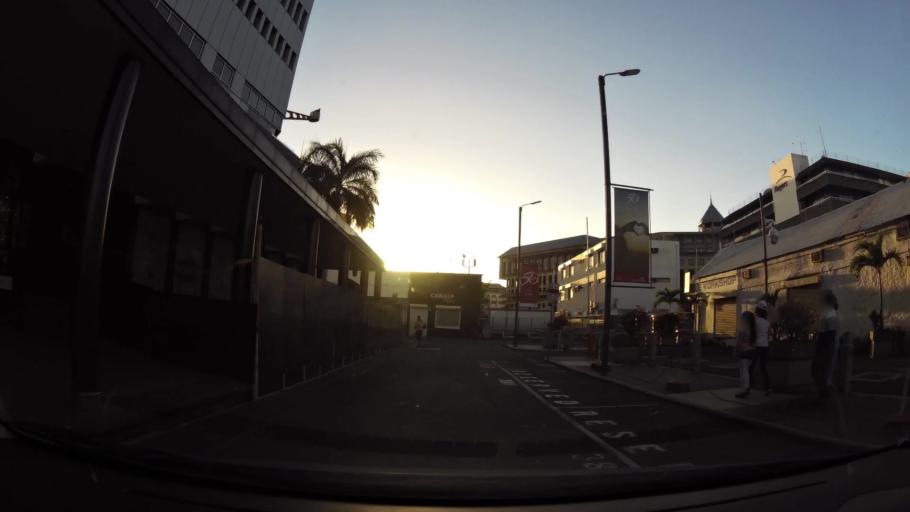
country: MU
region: Port Louis
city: Port Louis
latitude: -20.1629
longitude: 57.5007
